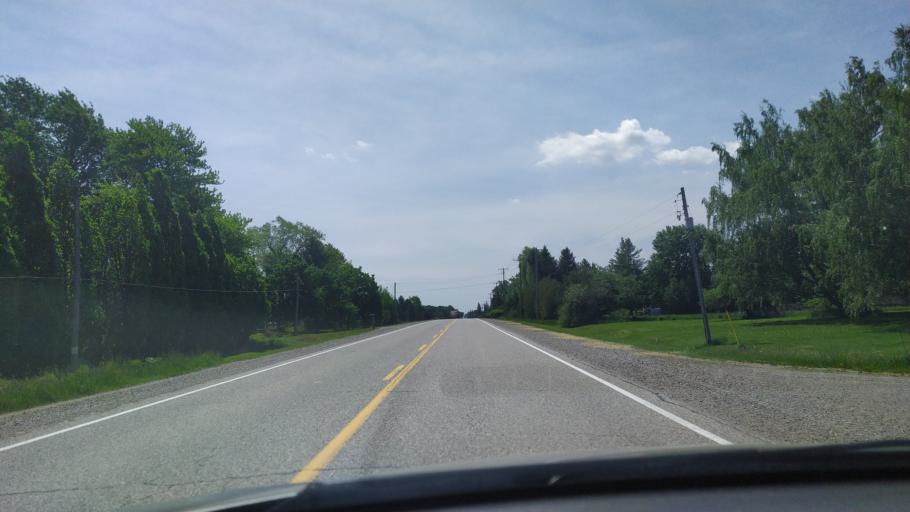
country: CA
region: Ontario
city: Dorchester
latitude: 43.1092
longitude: -81.0150
